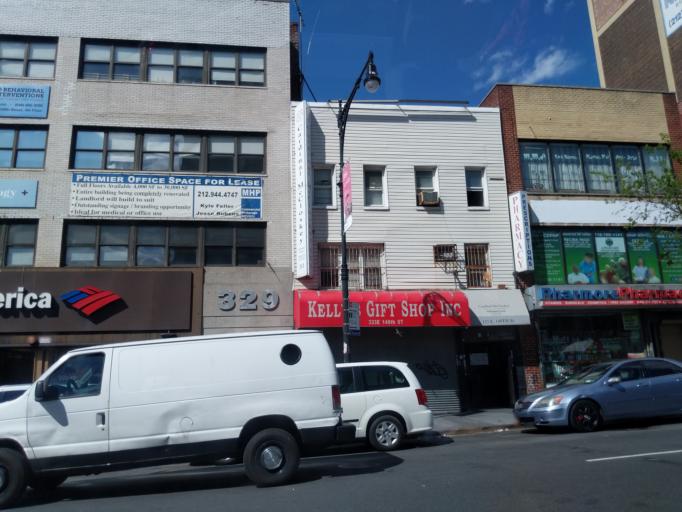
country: US
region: New York
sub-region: New York County
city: Inwood
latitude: 40.8168
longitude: -73.9203
